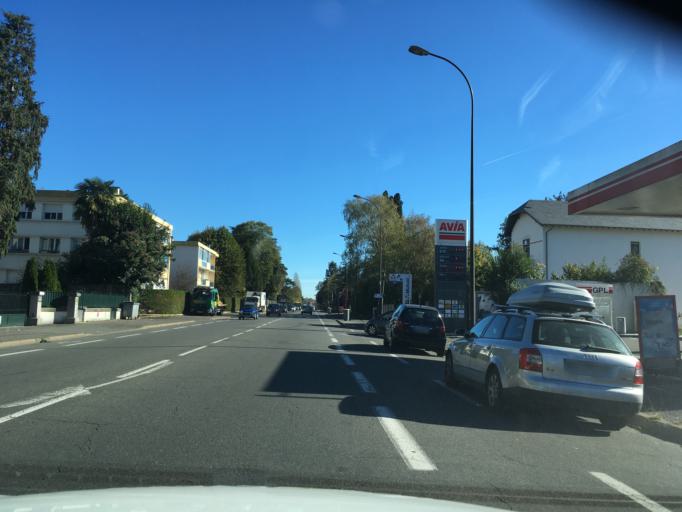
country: FR
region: Aquitaine
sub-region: Departement des Pyrenees-Atlantiques
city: Pau
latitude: 43.3035
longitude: -0.3478
